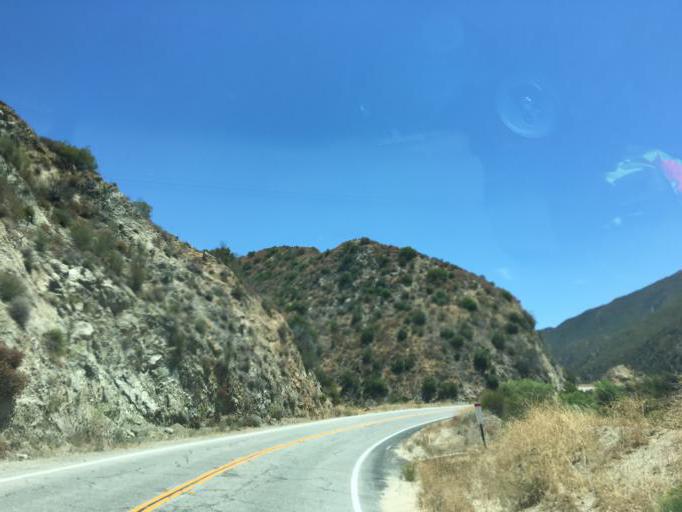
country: US
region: California
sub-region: Los Angeles County
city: La Crescenta-Montrose
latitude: 34.2936
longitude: -118.2342
